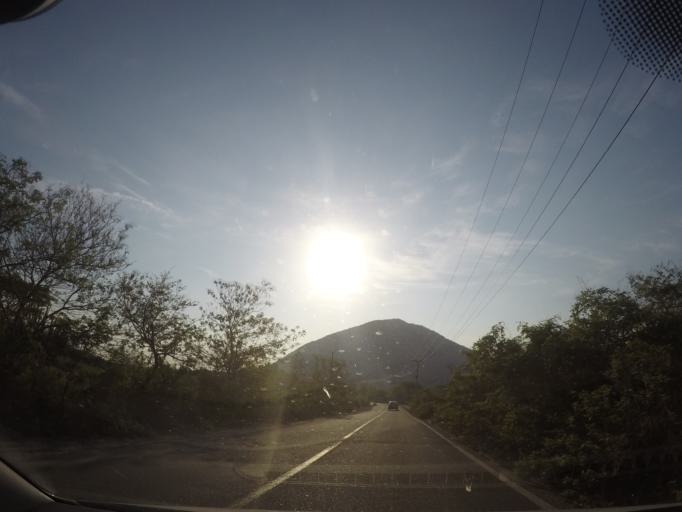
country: MX
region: Oaxaca
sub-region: Santo Domingo Tehuantepec
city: La Noria
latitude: 16.2367
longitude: -95.1622
